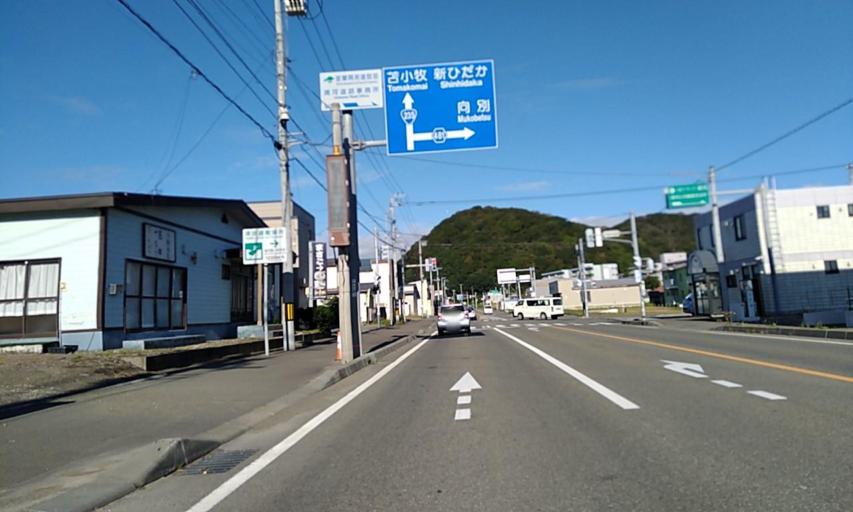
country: JP
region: Hokkaido
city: Shizunai-furukawacho
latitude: 42.1749
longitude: 142.7608
